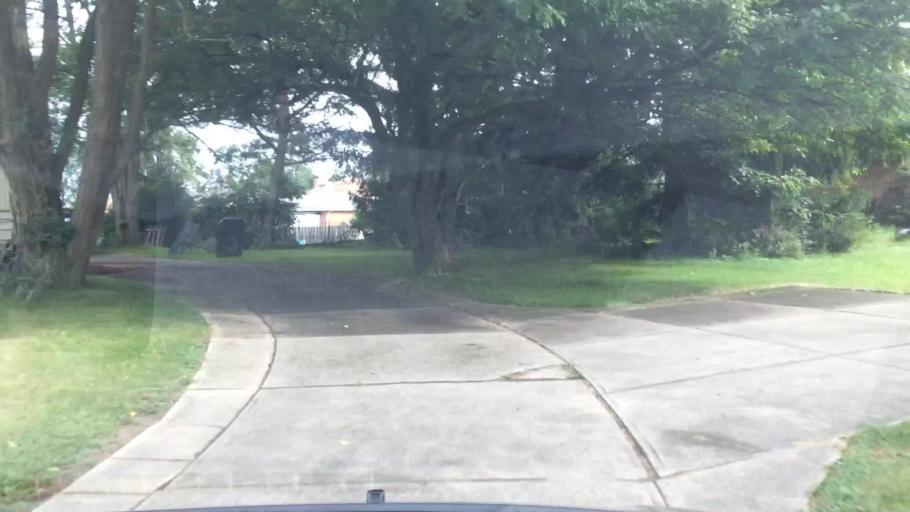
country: US
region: Ohio
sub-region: Cuyahoga County
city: Middleburg Heights
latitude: 41.3470
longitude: -81.8288
